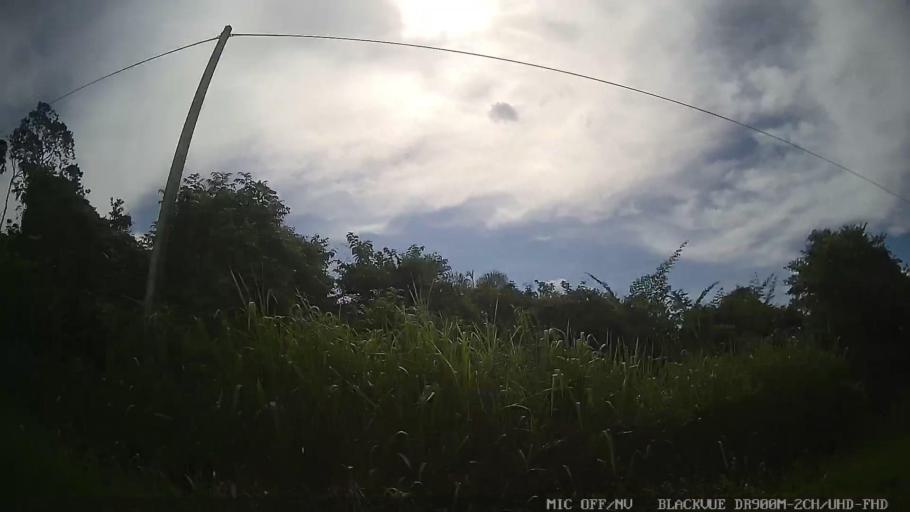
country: BR
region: Sao Paulo
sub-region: Conchas
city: Conchas
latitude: -22.9620
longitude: -47.9815
